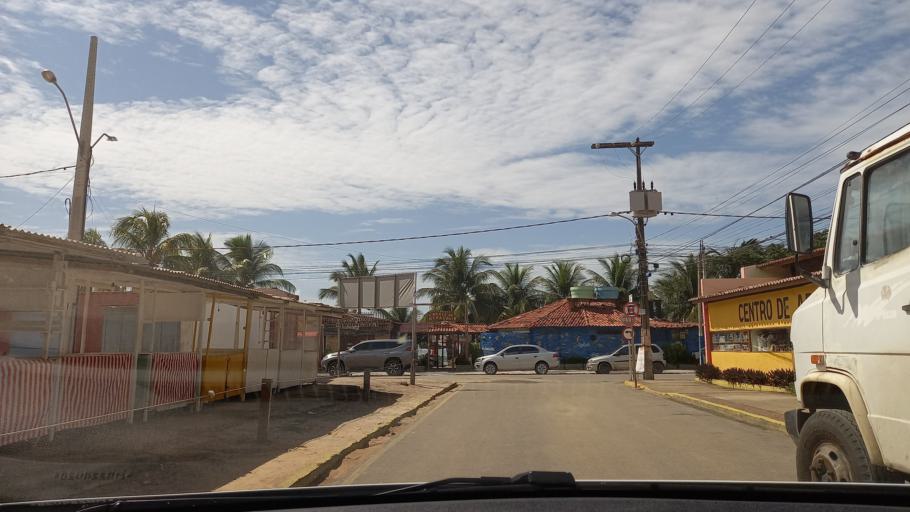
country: BR
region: Alagoas
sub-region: Maragogi
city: Maragogi
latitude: -9.0121
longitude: -35.2208
